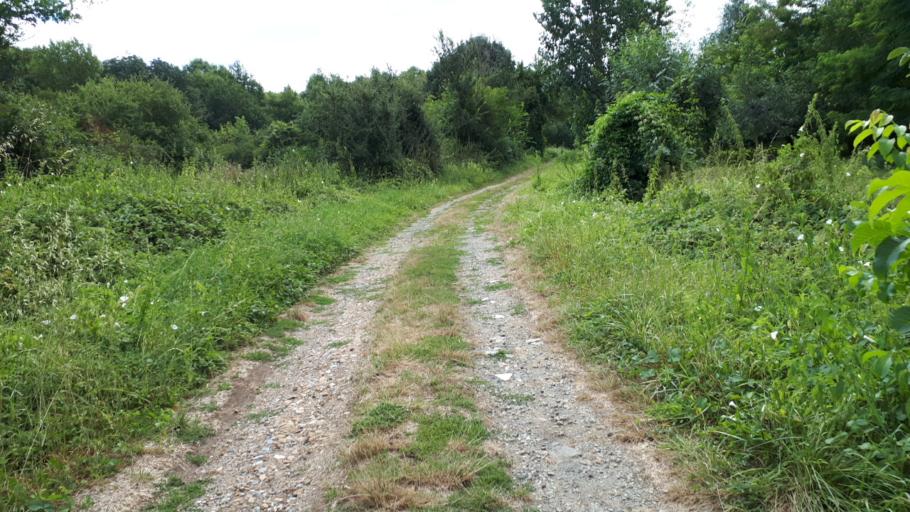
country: FR
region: Pays de la Loire
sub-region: Departement de Maine-et-Loire
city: Rochefort-sur-Loire
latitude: 47.3328
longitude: -0.6896
